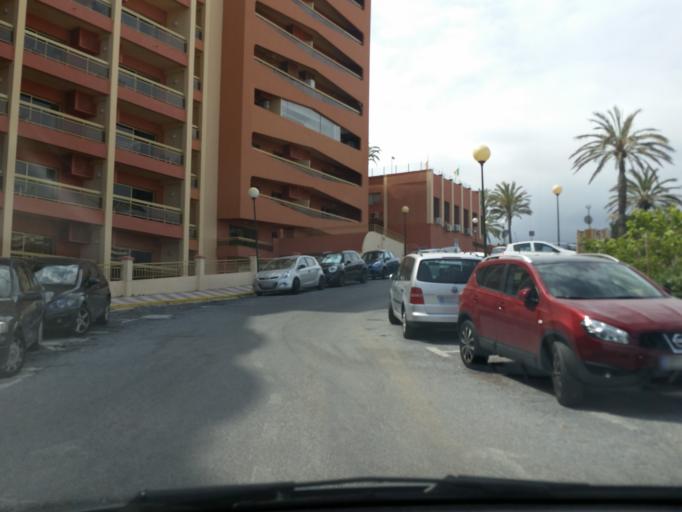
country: ES
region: Andalusia
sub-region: Provincia de Malaga
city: Benalmadena
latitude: 36.5827
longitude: -4.5343
